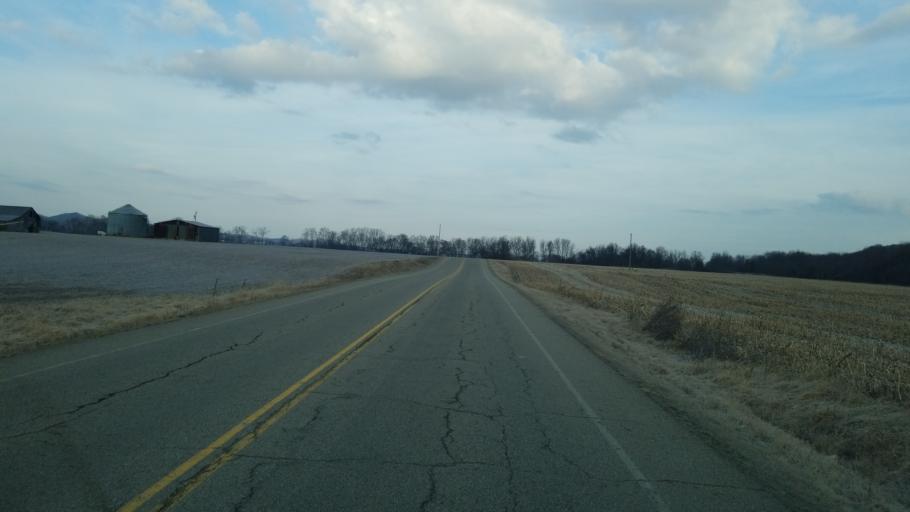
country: US
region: Ohio
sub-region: Pike County
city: Waverly
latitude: 39.2248
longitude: -82.8520
